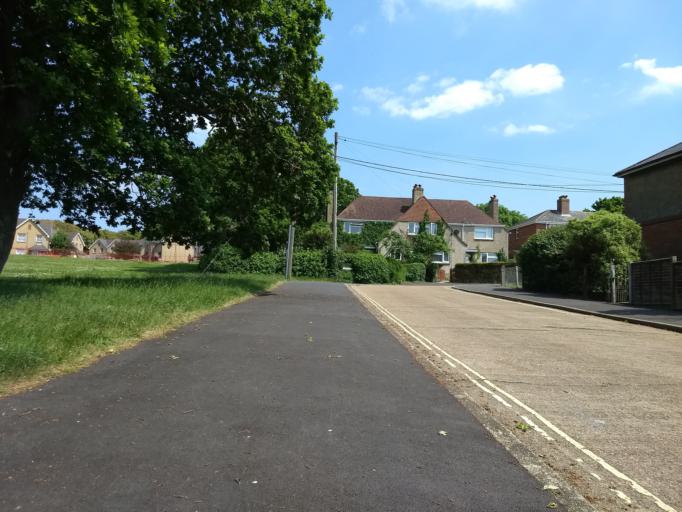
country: GB
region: England
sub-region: Isle of Wight
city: East Cowes
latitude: 50.7502
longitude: -1.2832
